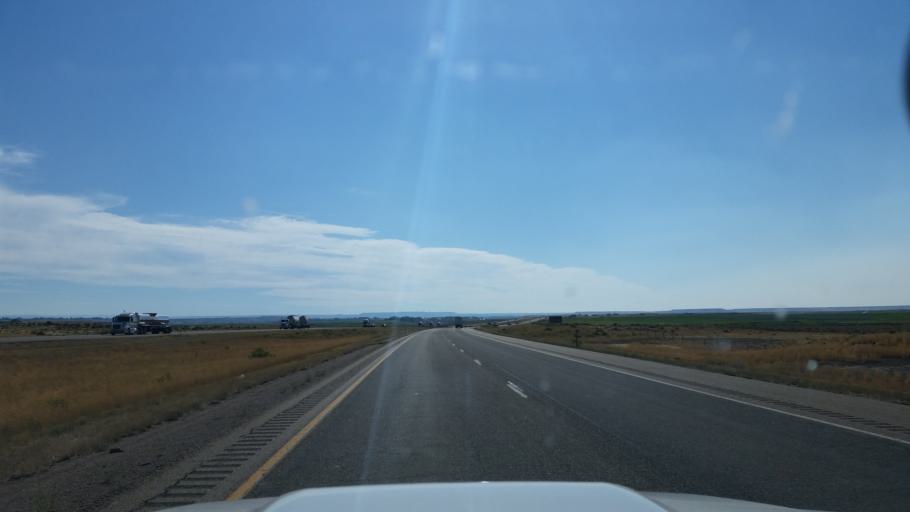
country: US
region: Wyoming
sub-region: Uinta County
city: Lyman
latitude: 41.3763
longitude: -110.2399
